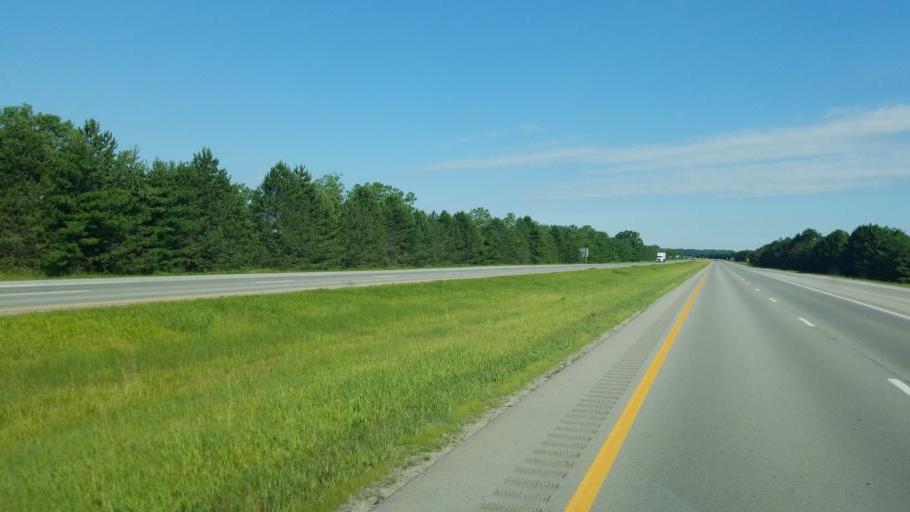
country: US
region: Ohio
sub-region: Wyandot County
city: Carey
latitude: 40.9718
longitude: -83.4865
